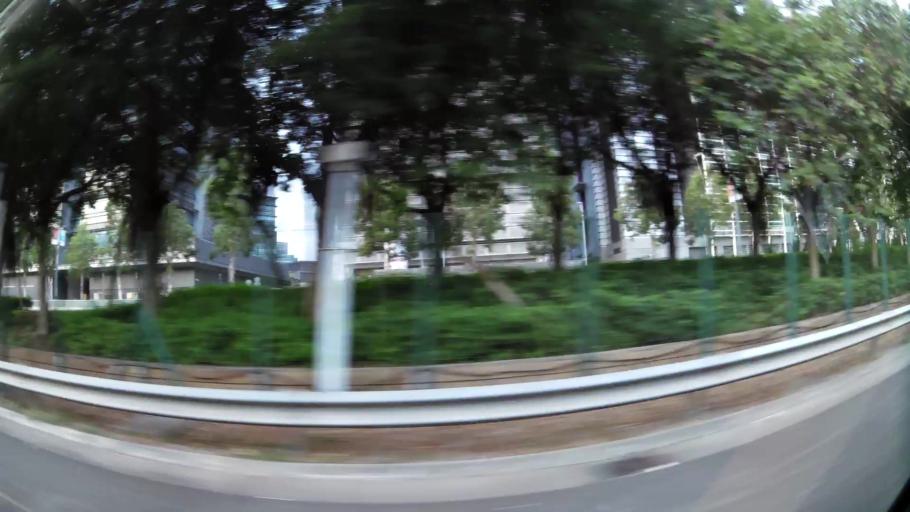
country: HK
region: Tai Po
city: Tai Po
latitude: 22.4255
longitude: 114.2095
